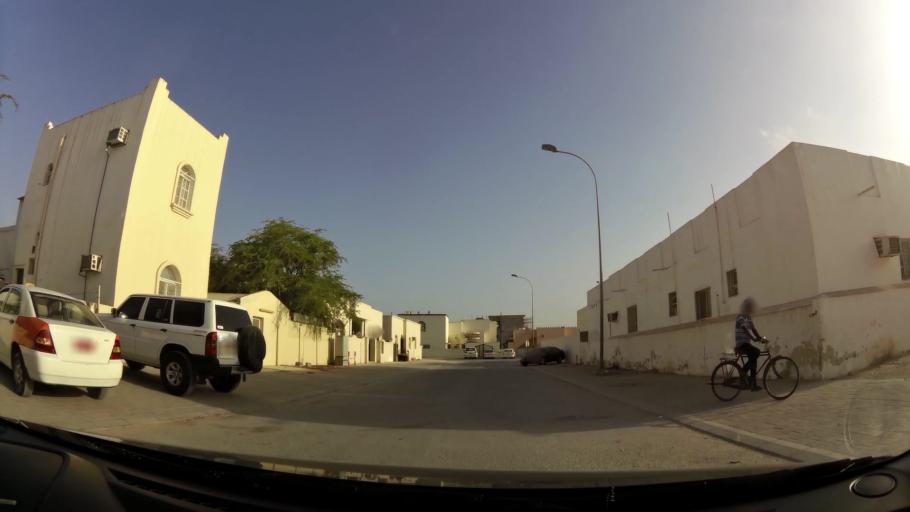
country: OM
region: Zufar
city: Salalah
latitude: 17.0082
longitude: 54.0313
